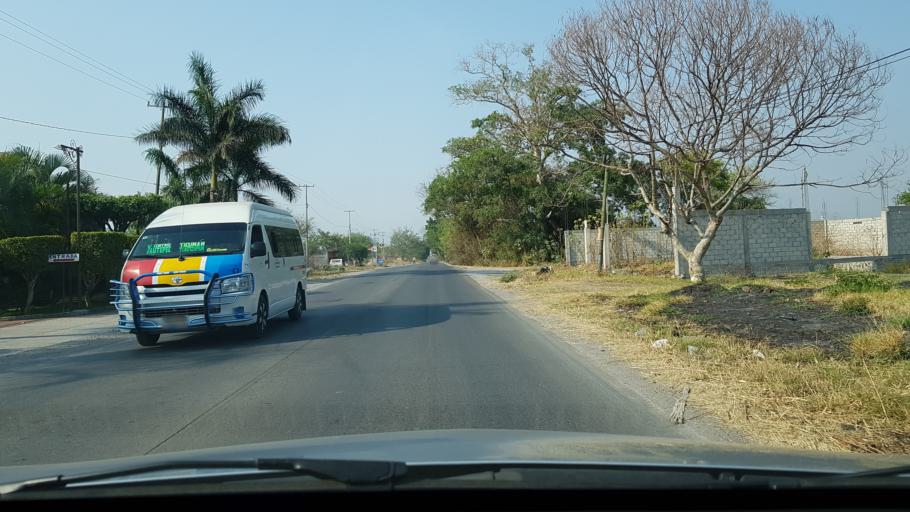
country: MX
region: Morelos
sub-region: Tlaquiltenango
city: Alfredo V. Bonfil (Chacampalco)
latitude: 18.6659
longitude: -99.1478
